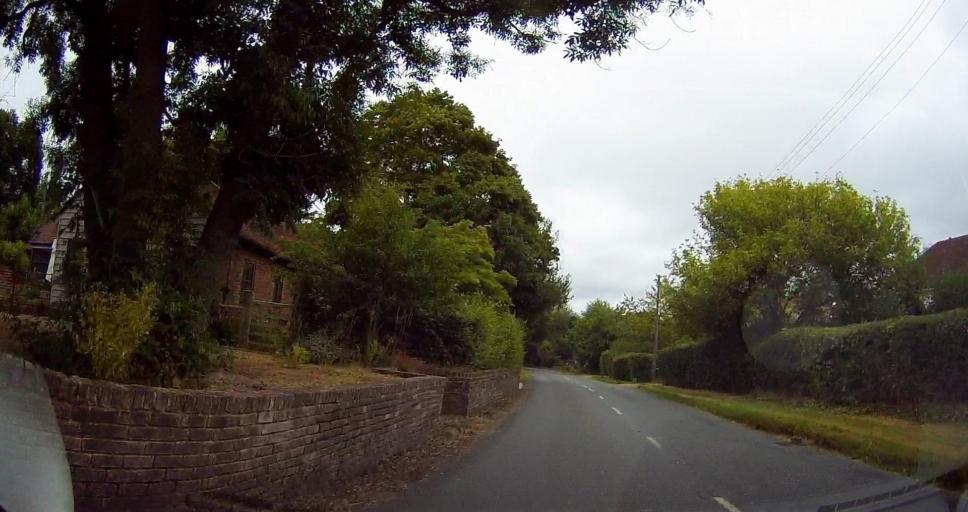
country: GB
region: England
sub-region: East Sussex
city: Wadhurst
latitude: 51.0761
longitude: 0.3554
